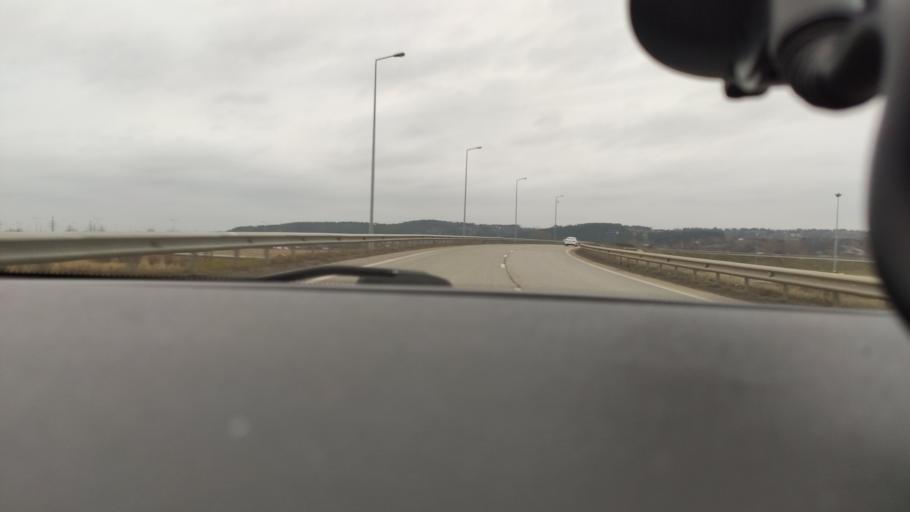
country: RU
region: Perm
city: Kondratovo
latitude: 57.9272
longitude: 56.1728
